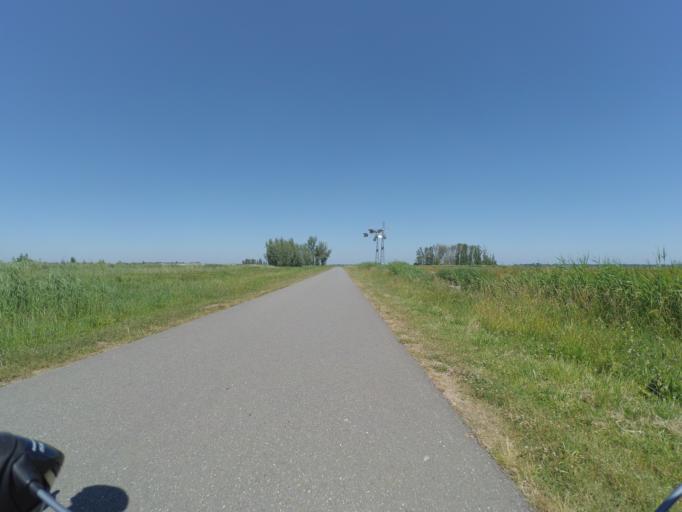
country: NL
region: South Holland
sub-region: Gemeente Hardinxveld-Giessendam
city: Neder-Hardinxveld
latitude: 51.7810
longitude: 4.8400
